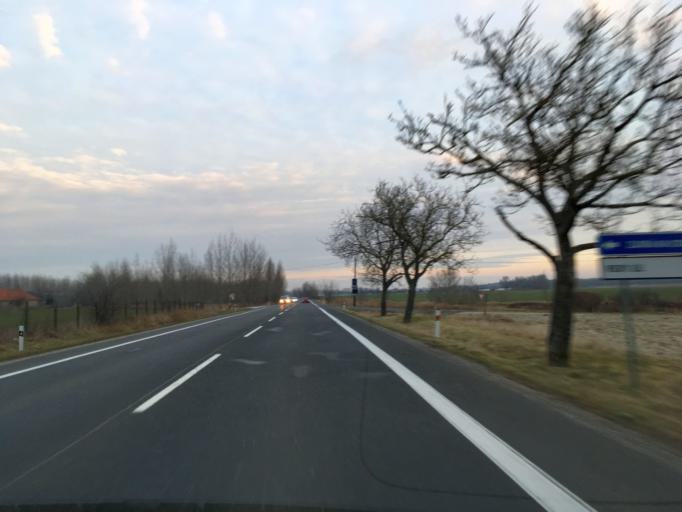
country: HU
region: Komarom-Esztergom
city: Acs
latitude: 47.7703
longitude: 17.9606
